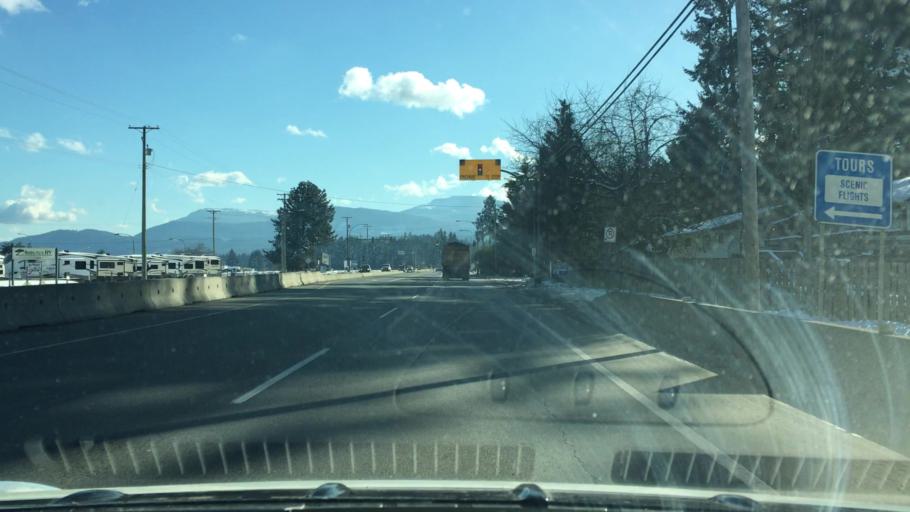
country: CA
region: British Columbia
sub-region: Cowichan Valley Regional District
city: Ladysmith
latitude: 49.0555
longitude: -123.8776
